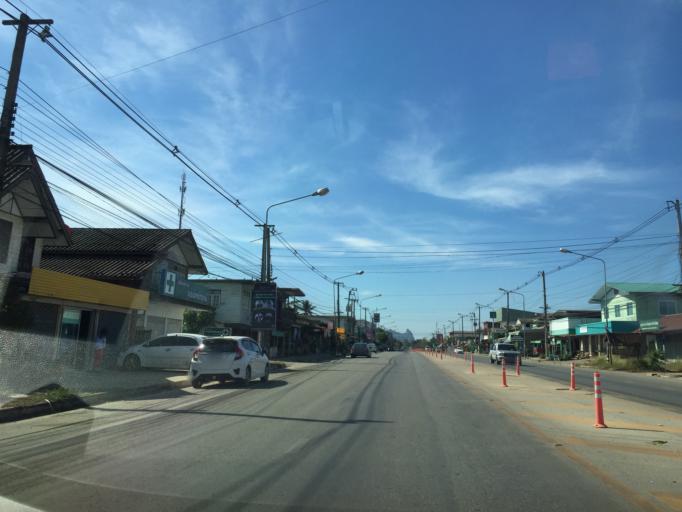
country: TH
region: Changwat Nong Bua Lamphu
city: Na Wang
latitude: 17.3229
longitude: 102.0849
